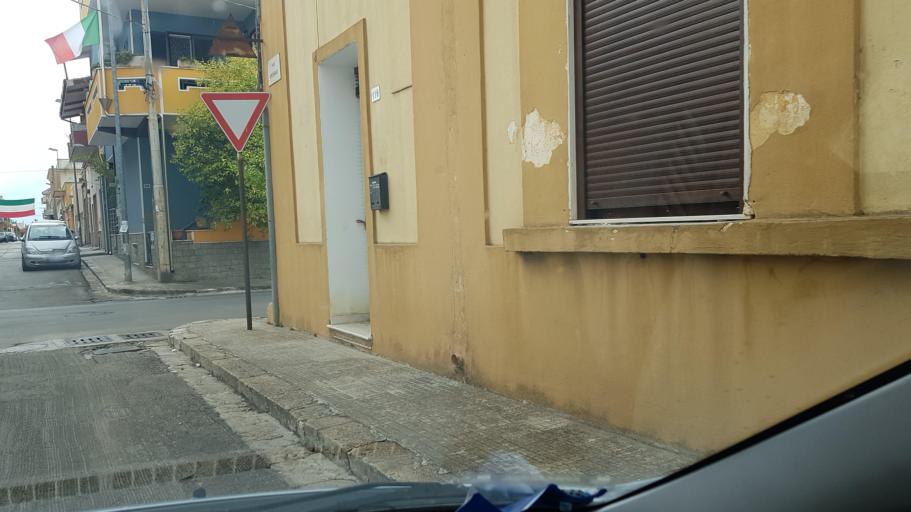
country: IT
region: Apulia
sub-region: Provincia di Lecce
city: Taurisano
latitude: 39.9528
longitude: 18.2179
